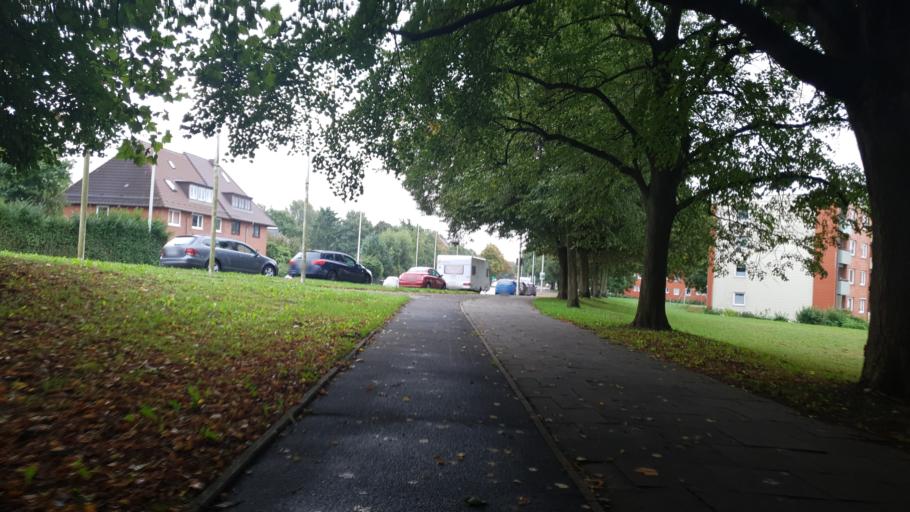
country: DE
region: Schleswig-Holstein
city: Kronshagen
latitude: 54.3606
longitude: 10.0783
